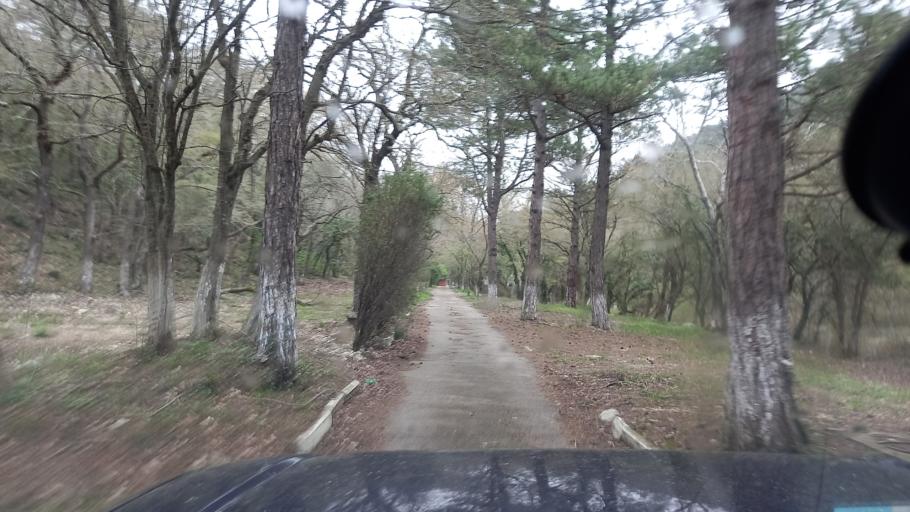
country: RU
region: Krasnodarskiy
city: Arkhipo-Osipovka
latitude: 44.3703
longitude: 38.4498
